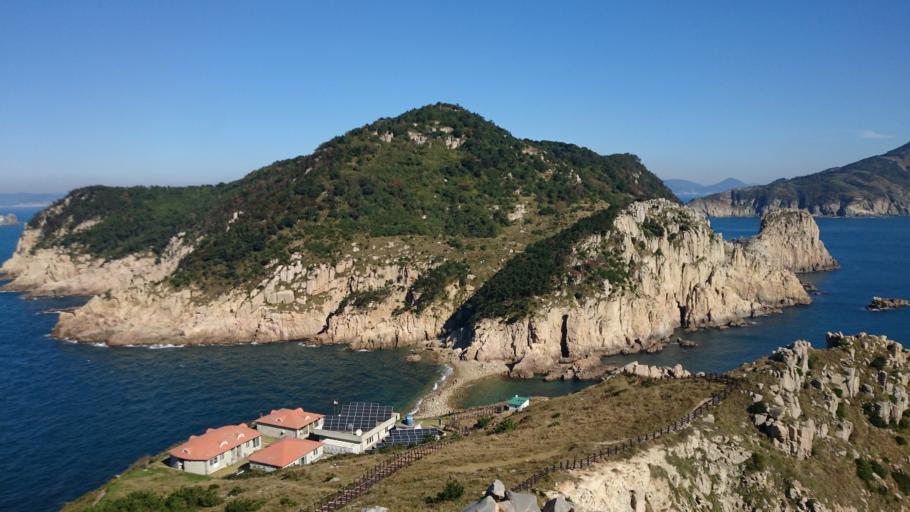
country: KR
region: Gyeongsangnam-do
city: Kyosai
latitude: 34.6197
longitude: 128.5479
